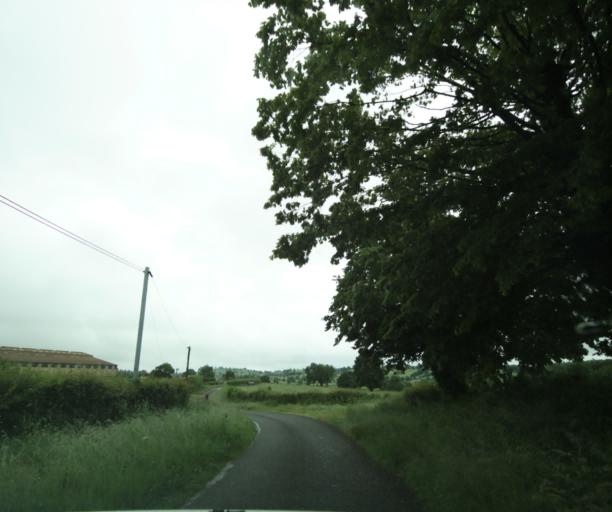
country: FR
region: Bourgogne
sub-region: Departement de Saone-et-Loire
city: La Clayette
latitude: 46.3483
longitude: 4.2312
